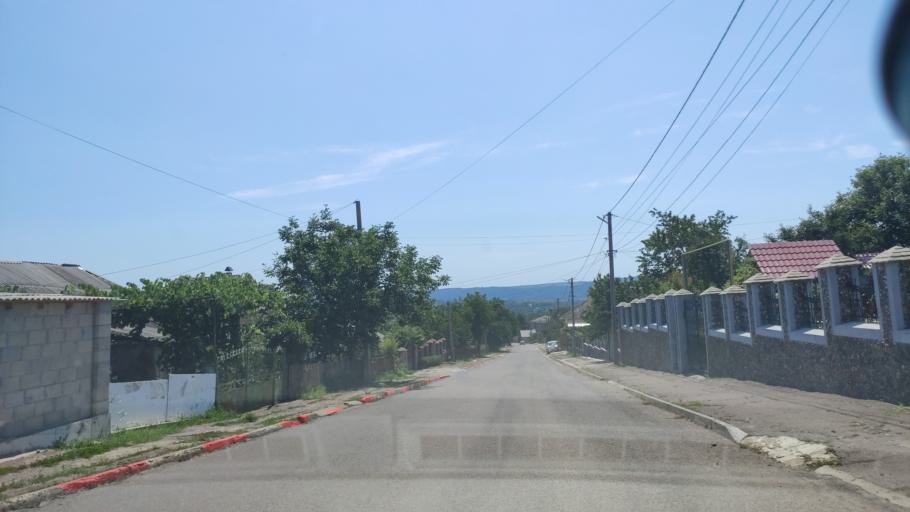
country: MD
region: Raionul Soroca
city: Soroca
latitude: 48.1707
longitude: 28.2979
